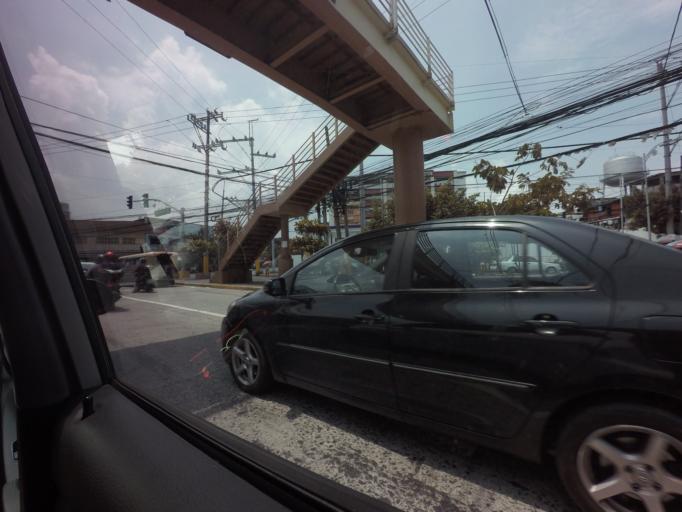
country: PH
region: Metro Manila
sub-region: City of Manila
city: Quiapo
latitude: 14.5962
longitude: 120.9895
